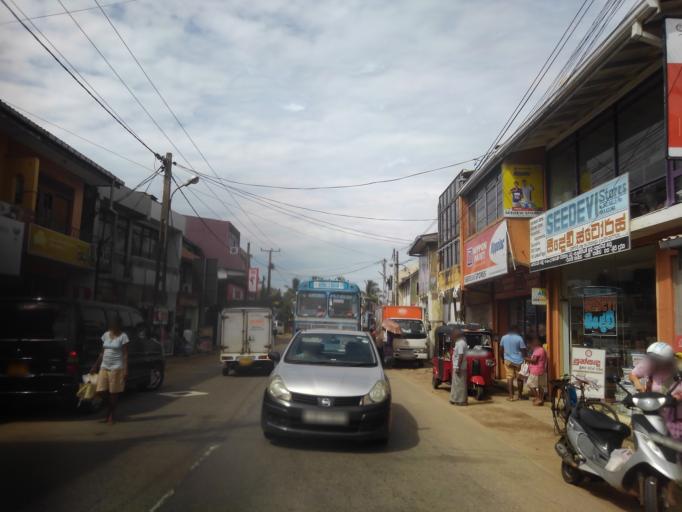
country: LK
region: Southern
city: Hikkaduwa
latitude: 6.1408
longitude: 80.0997
